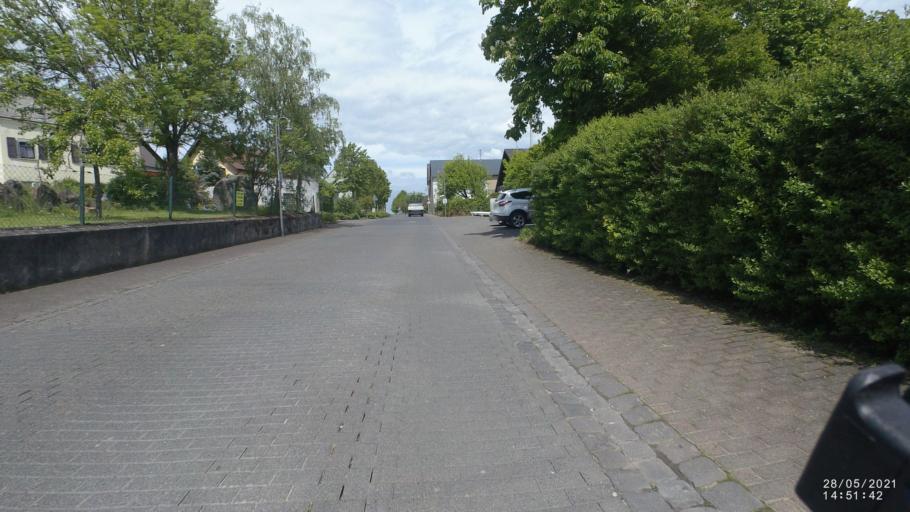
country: DE
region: Rheinland-Pfalz
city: Pillig
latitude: 50.2413
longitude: 7.3137
